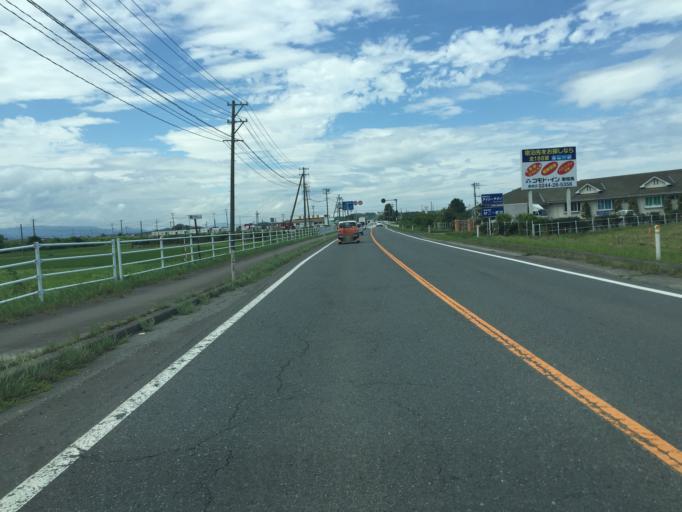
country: JP
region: Fukushima
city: Namie
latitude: 37.6912
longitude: 140.9757
